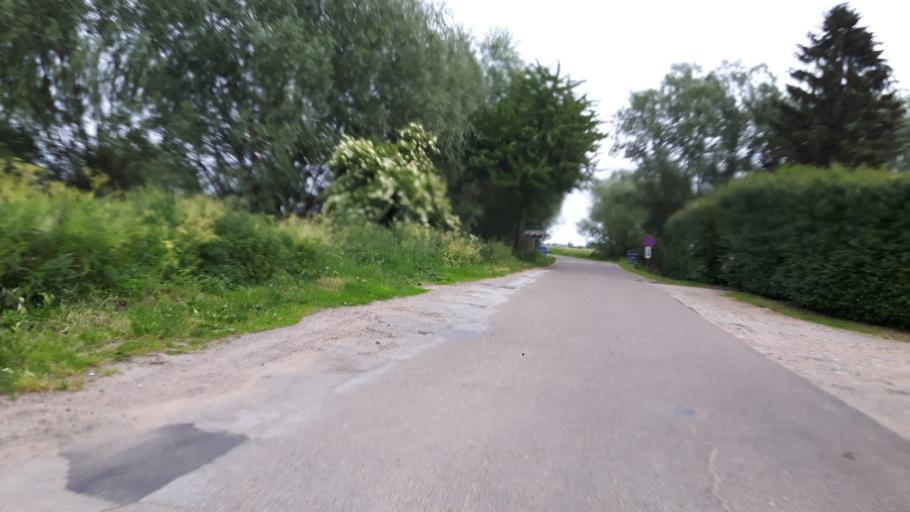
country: PL
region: Pomeranian Voivodeship
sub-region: Powiat nowodworski
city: Sztutowo
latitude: 54.2659
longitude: 19.1689
